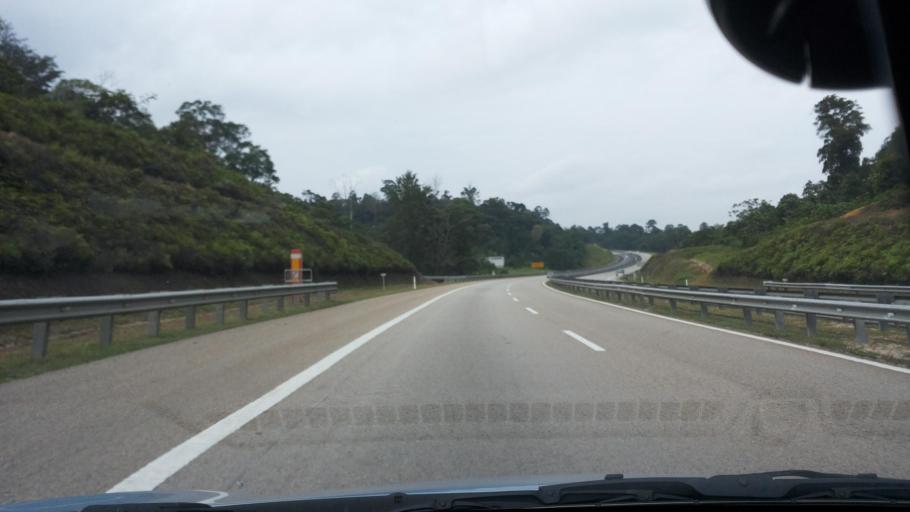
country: MY
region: Pahang
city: Kuantan
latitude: 3.7599
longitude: 103.1337
